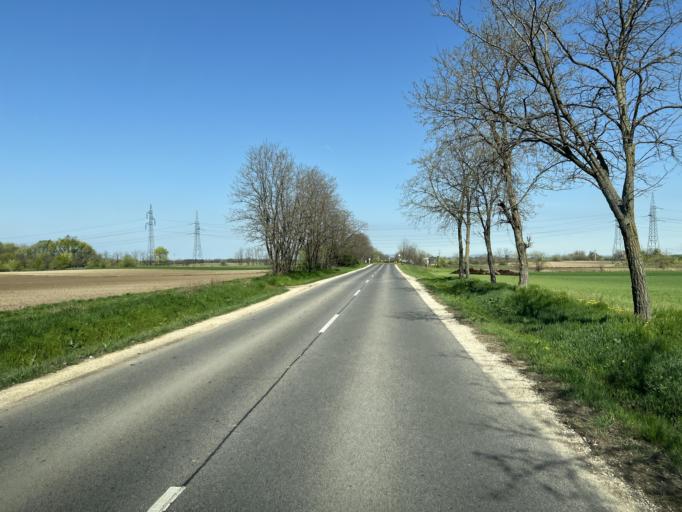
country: HU
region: Pest
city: Ocsa
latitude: 47.3139
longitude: 19.2047
